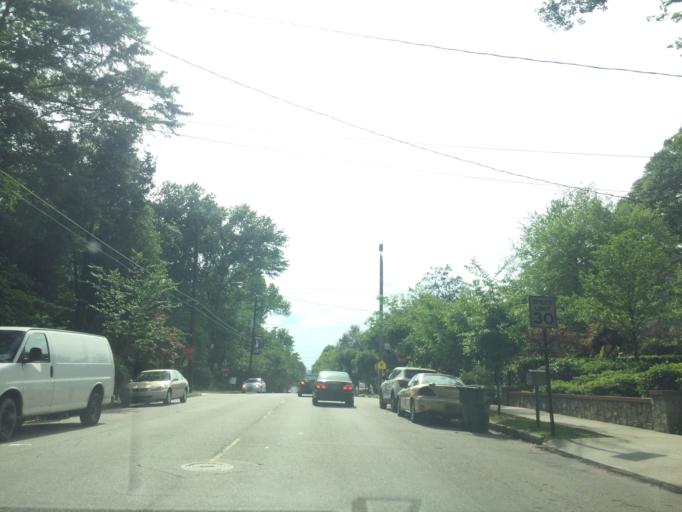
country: US
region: Georgia
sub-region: DeKalb County
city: Druid Hills
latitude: 33.7822
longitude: -84.3580
